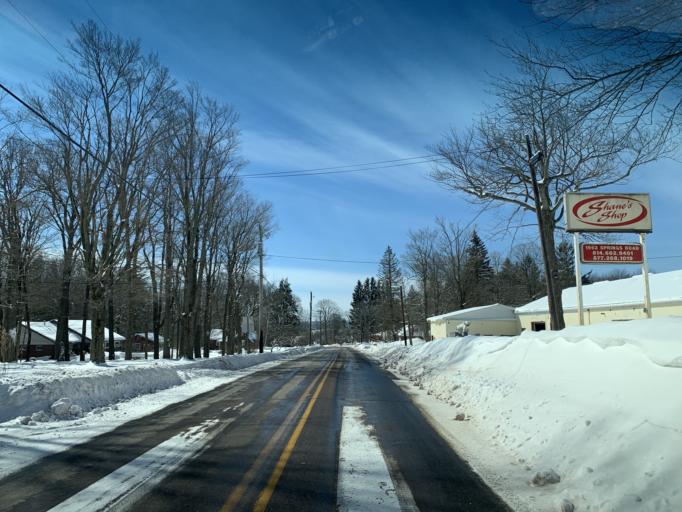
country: US
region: Pennsylvania
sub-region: Somerset County
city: Meyersdale
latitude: 39.7284
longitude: -79.1566
